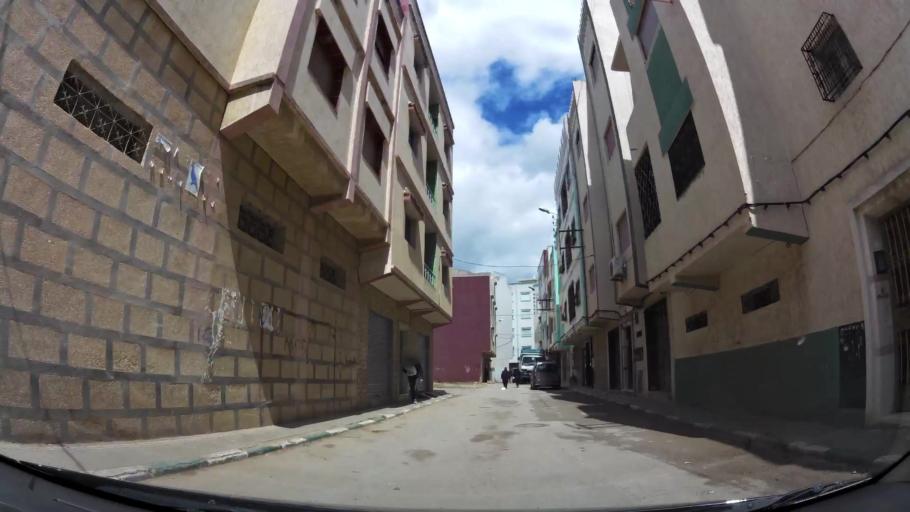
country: MA
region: Tanger-Tetouan
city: Tetouan
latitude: 35.5770
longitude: -5.3530
